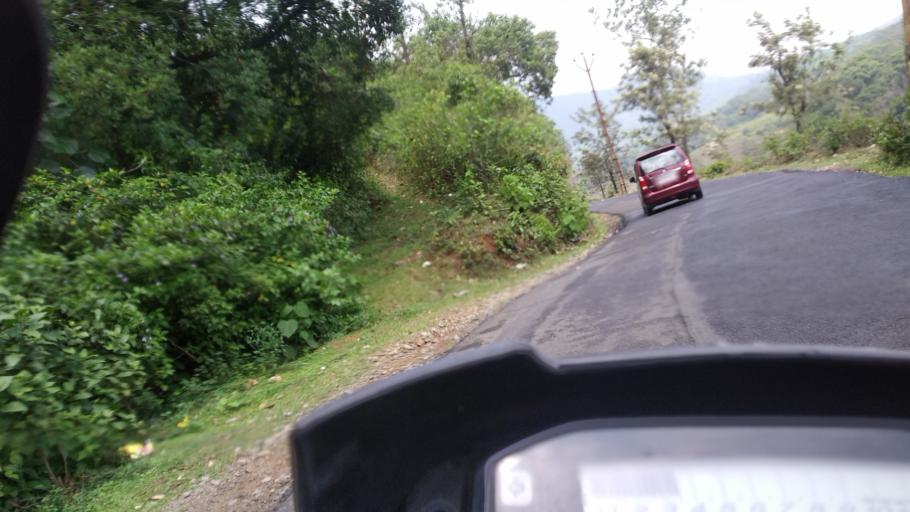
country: IN
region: Kerala
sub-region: Kottayam
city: Erattupetta
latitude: 9.6330
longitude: 76.9606
